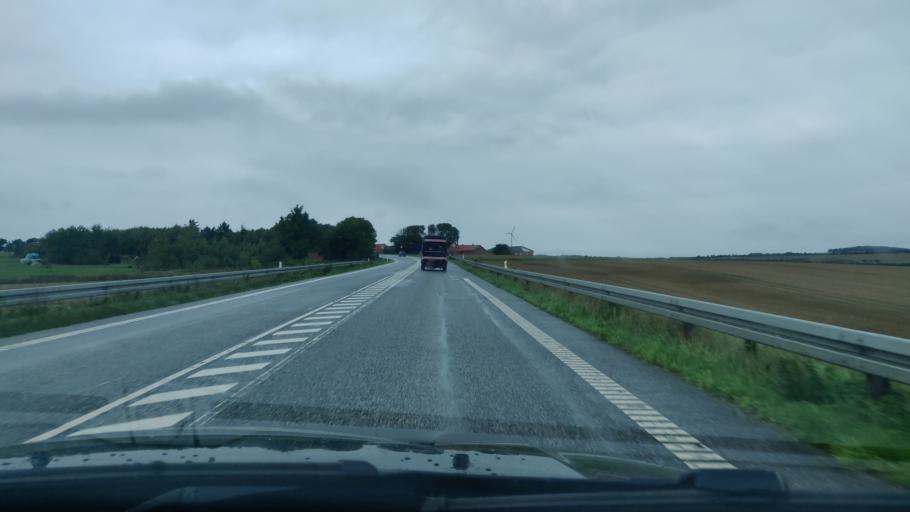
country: DK
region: North Denmark
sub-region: Thisted Kommune
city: Thisted
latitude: 56.9845
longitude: 8.7670
